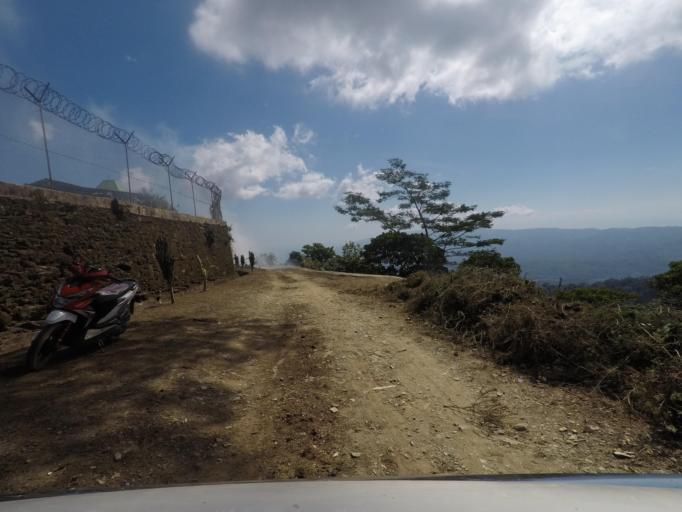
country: TL
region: Ermera
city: Gleno
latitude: -8.7527
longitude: 125.3249
